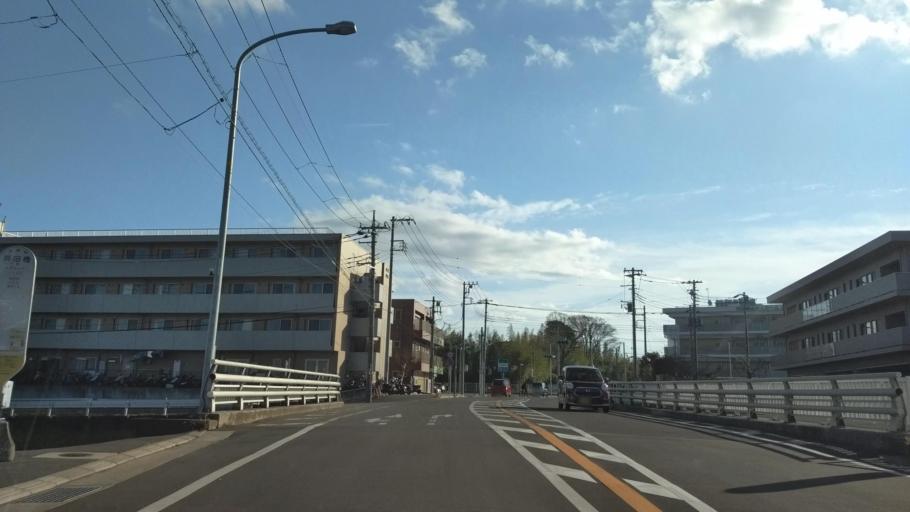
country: JP
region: Kanagawa
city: Isehara
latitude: 35.3734
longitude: 139.2839
